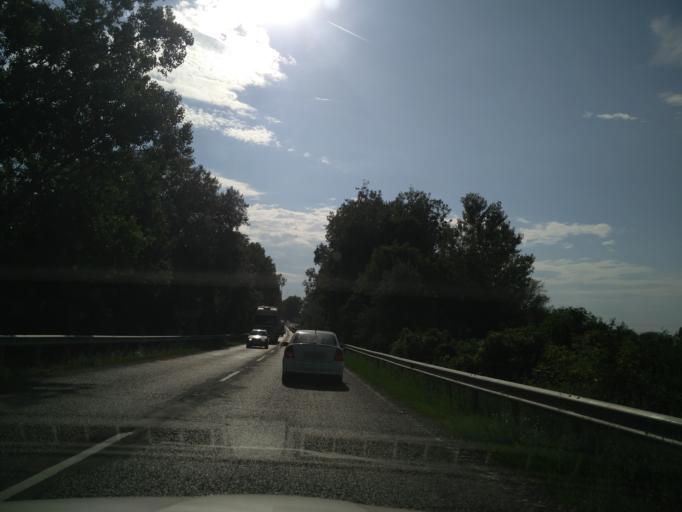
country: HU
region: Fejer
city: Bicske
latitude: 47.4948
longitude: 18.6894
